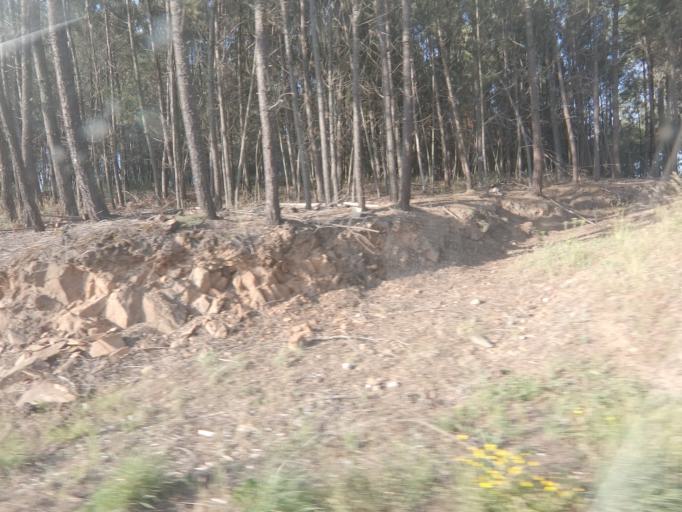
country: PT
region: Vila Real
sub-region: Vila Real
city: Vila Real
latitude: 41.2784
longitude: -7.6837
